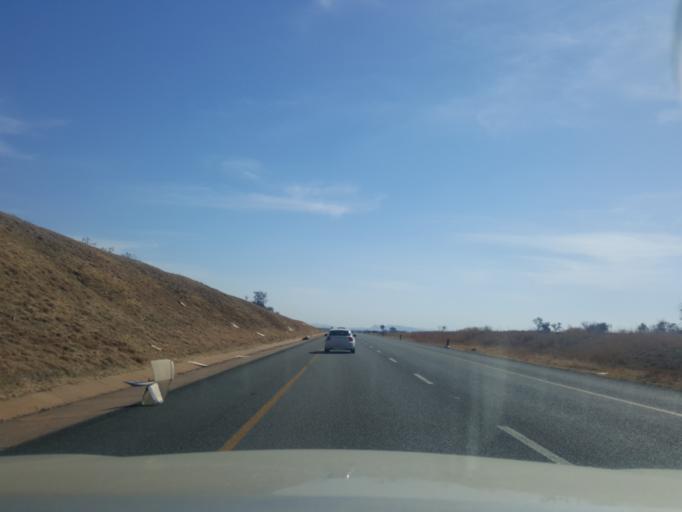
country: ZA
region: North-West
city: Ga-Rankuwa
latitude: -25.6556
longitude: 27.9901
